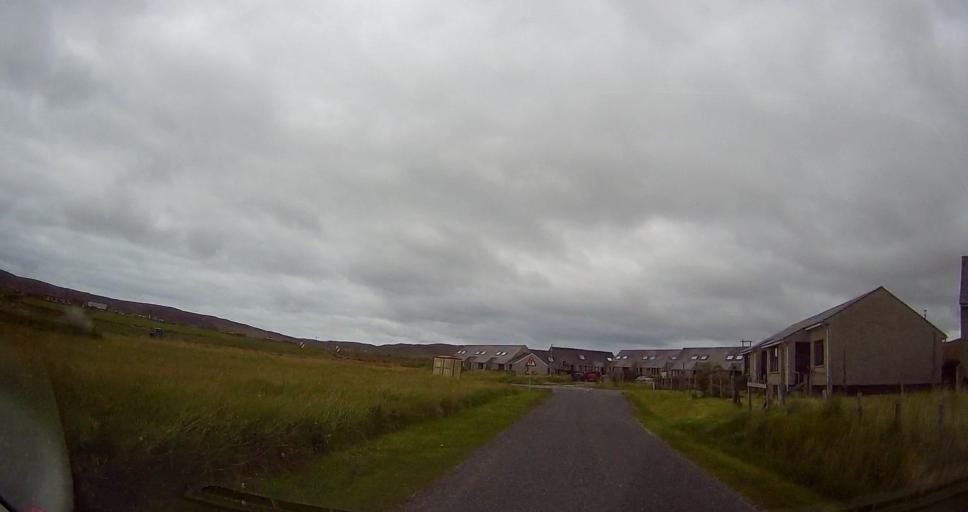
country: GB
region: Scotland
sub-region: Shetland Islands
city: Shetland
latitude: 60.7577
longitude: -0.8622
